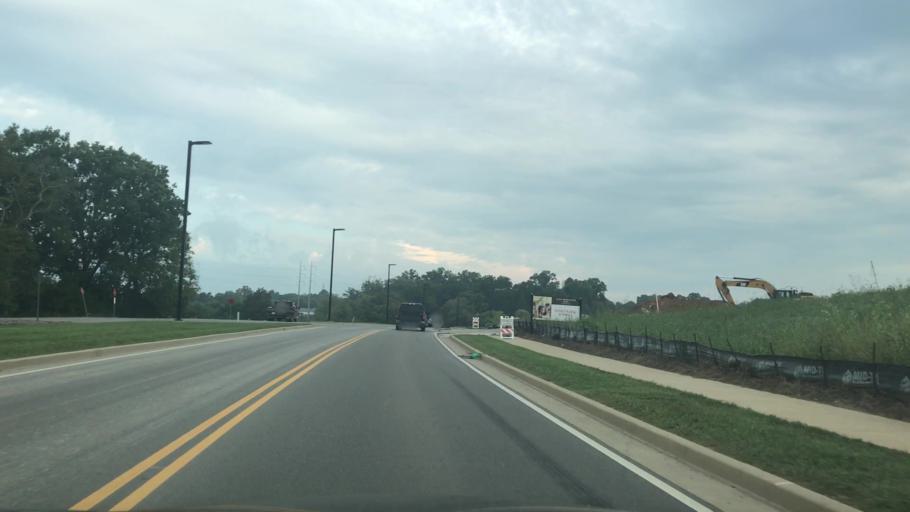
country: US
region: Tennessee
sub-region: Williamson County
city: Franklin
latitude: 35.8938
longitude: -86.8256
